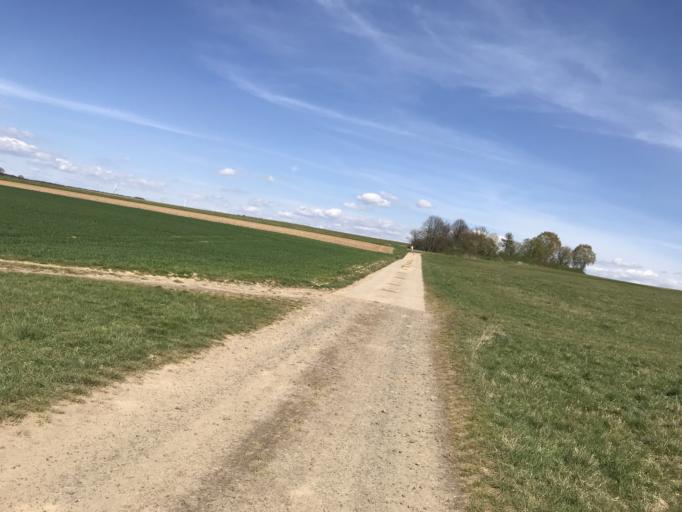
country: DE
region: Hesse
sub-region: Regierungsbezirk Giessen
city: Alten Buseck
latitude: 50.6515
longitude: 8.7698
